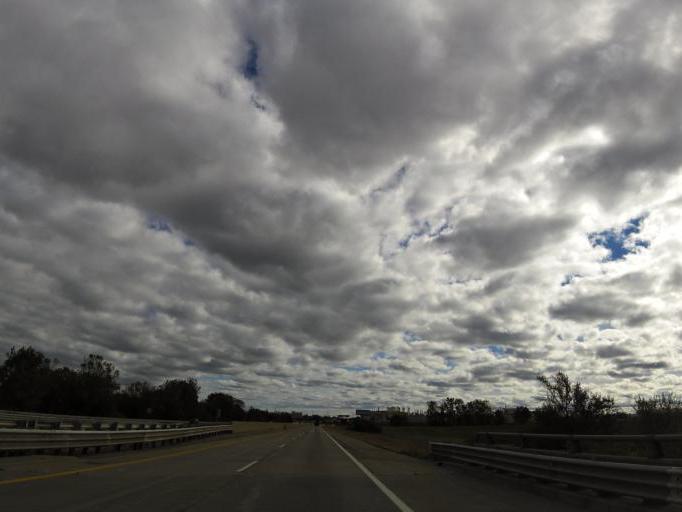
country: US
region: Michigan
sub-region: Genesee County
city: Flint
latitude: 42.9853
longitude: -83.7307
